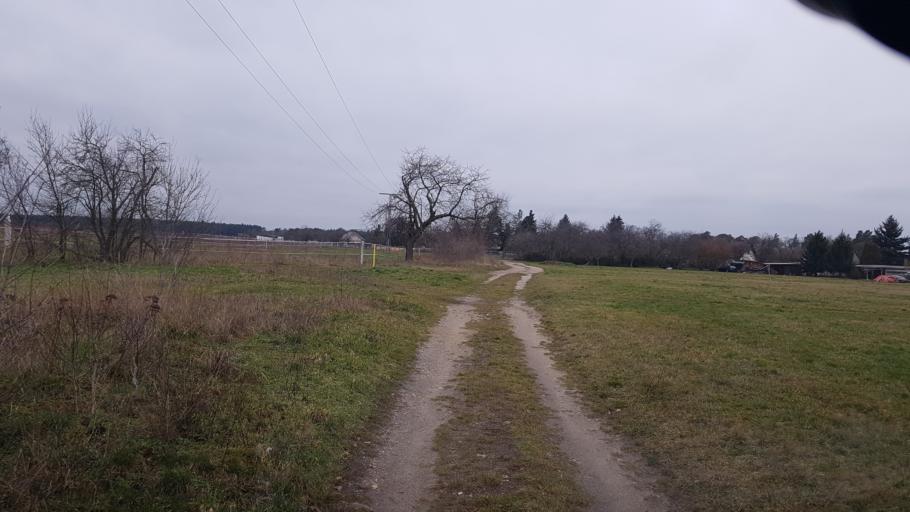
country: DE
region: Brandenburg
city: Crinitz
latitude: 51.7374
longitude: 13.7216
